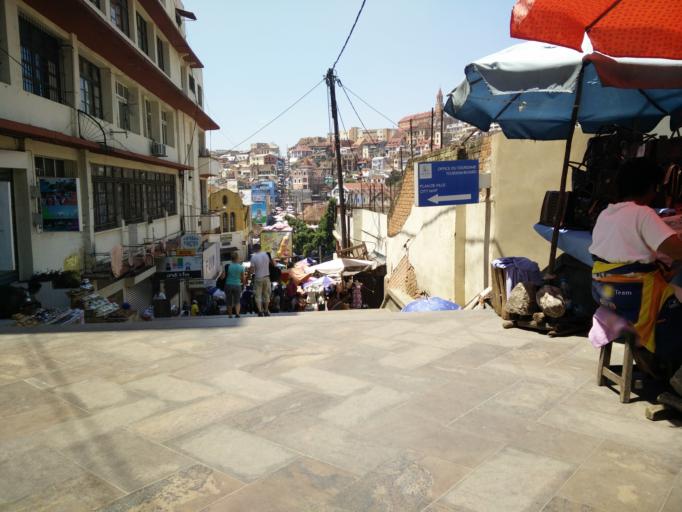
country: MG
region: Analamanga
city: Antananarivo
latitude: -18.9089
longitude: 47.5257
